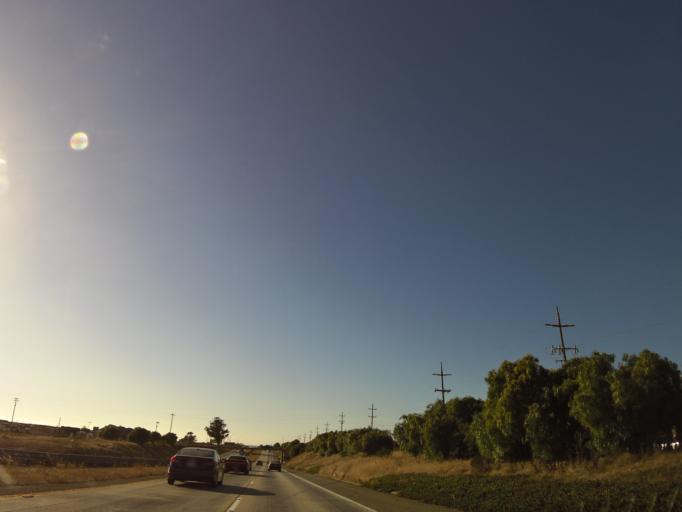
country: US
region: California
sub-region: Monterey County
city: Chualar
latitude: 36.5679
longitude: -121.5163
